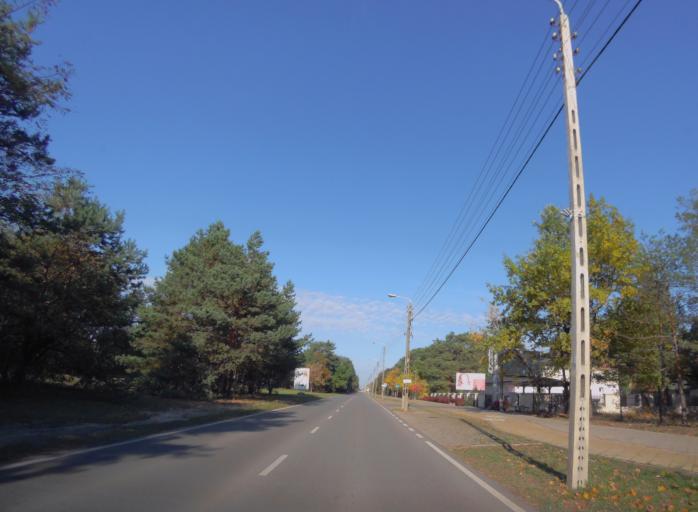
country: PL
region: Masovian Voivodeship
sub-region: Powiat otwocki
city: Jozefow
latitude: 52.1444
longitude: 21.2289
